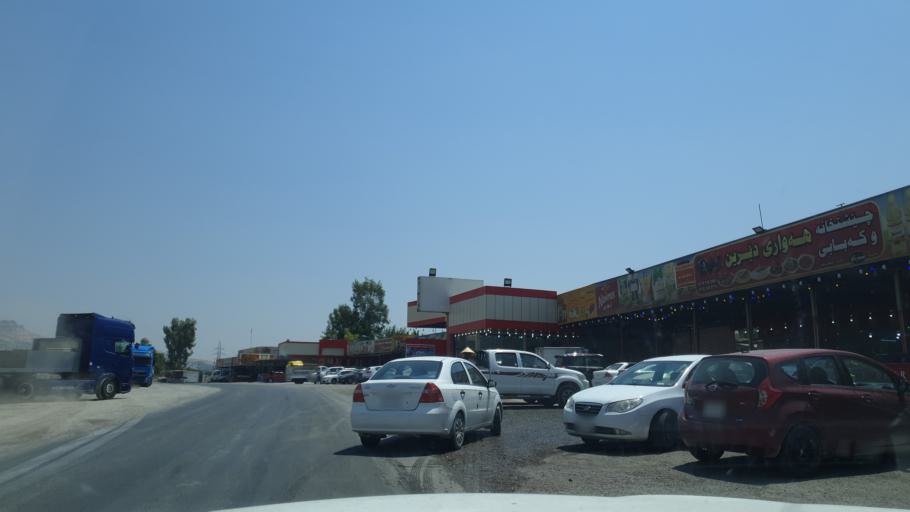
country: IQ
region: Arbil
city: Koysinceq
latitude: 36.0833
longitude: 44.7566
